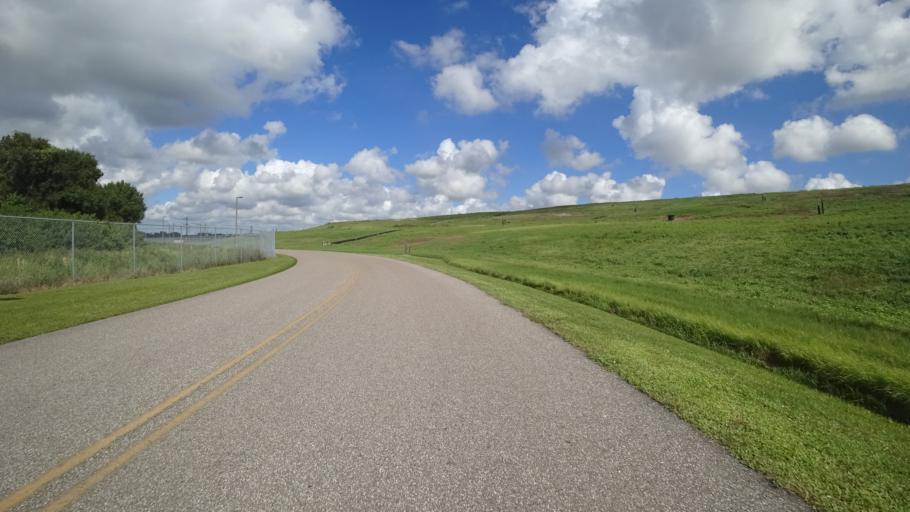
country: US
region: Florida
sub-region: Manatee County
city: Samoset
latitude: 27.4701
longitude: -82.4518
